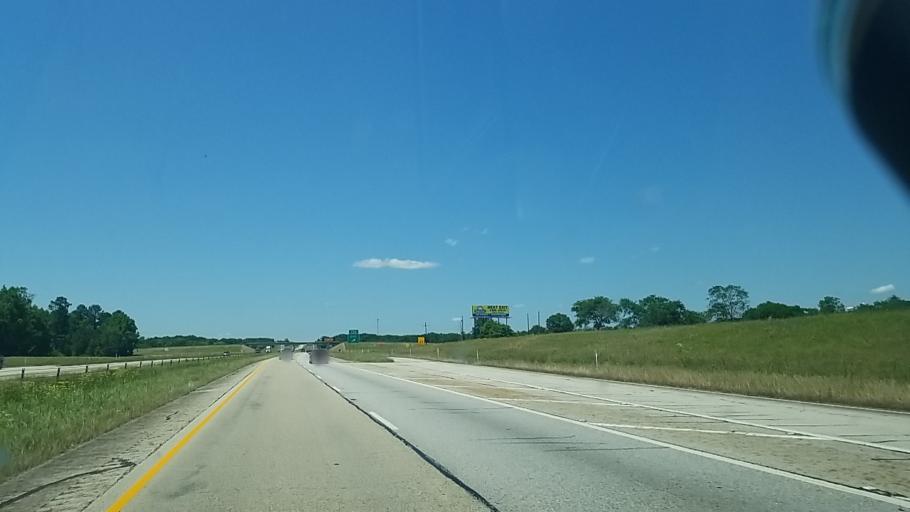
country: US
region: Texas
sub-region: Leon County
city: Centerville
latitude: 31.1448
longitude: -95.9818
